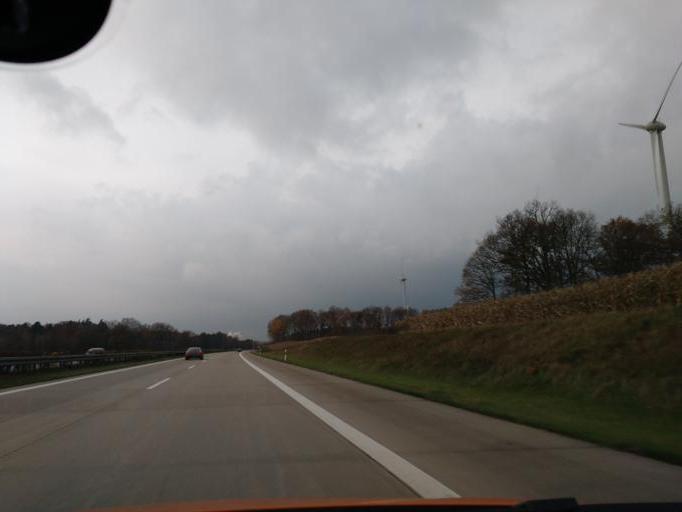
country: DE
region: Brandenburg
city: Wittstock
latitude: 53.1384
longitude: 12.4327
